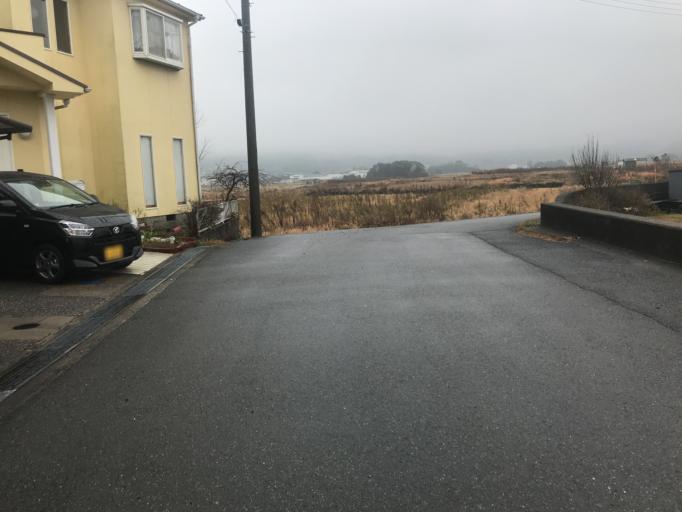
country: JP
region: Kyoto
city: Kameoka
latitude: 34.9951
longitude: 135.5430
